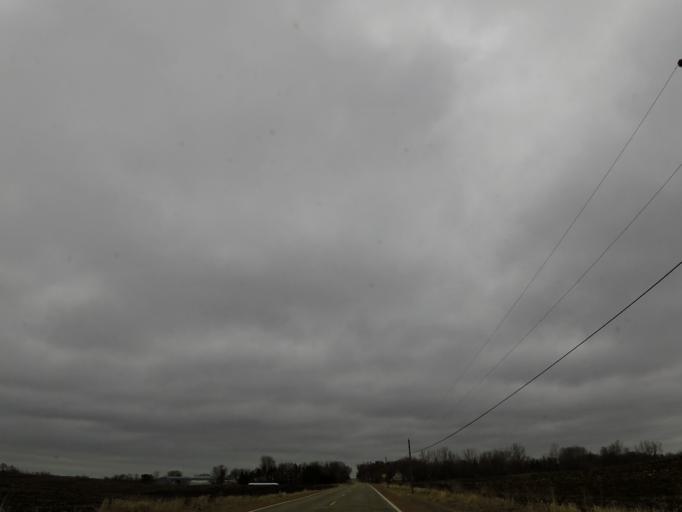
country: US
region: Minnesota
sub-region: Scott County
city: Shakopee
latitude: 44.7280
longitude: -93.5418
